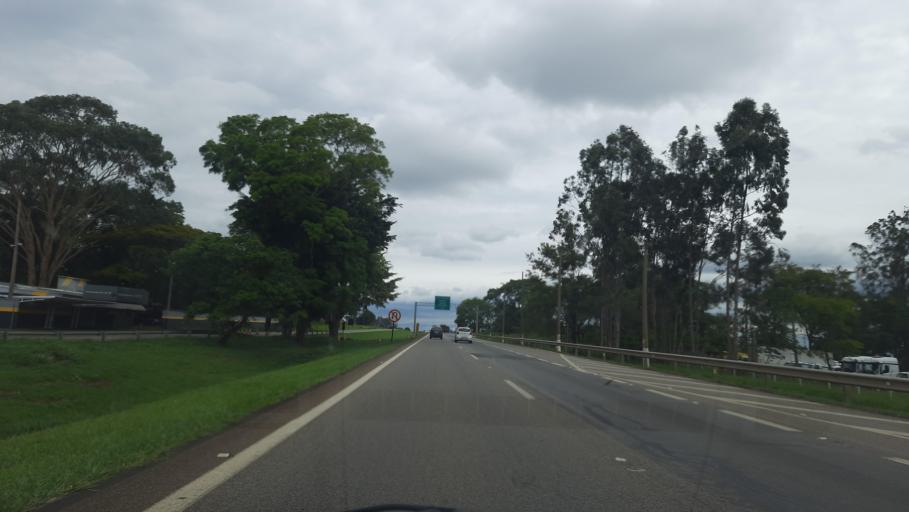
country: BR
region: Sao Paulo
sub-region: Mogi-Mirim
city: Mogi Mirim
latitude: -22.4620
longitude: -46.9823
